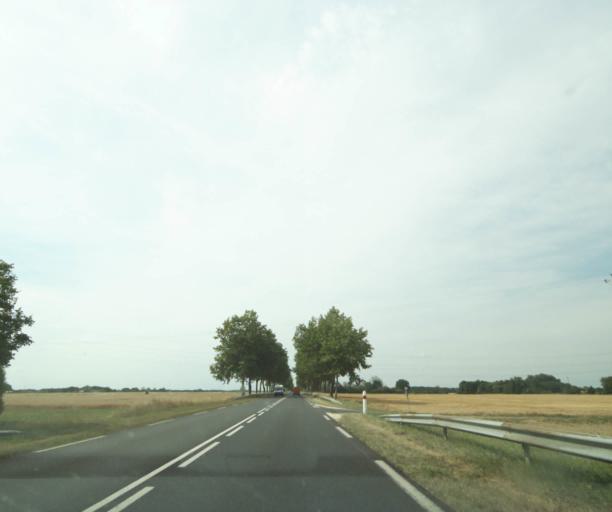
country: FR
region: Centre
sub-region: Departement d'Indre-et-Loire
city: Saint-Antoine-du-Rocher
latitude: 47.5105
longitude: 0.5925
